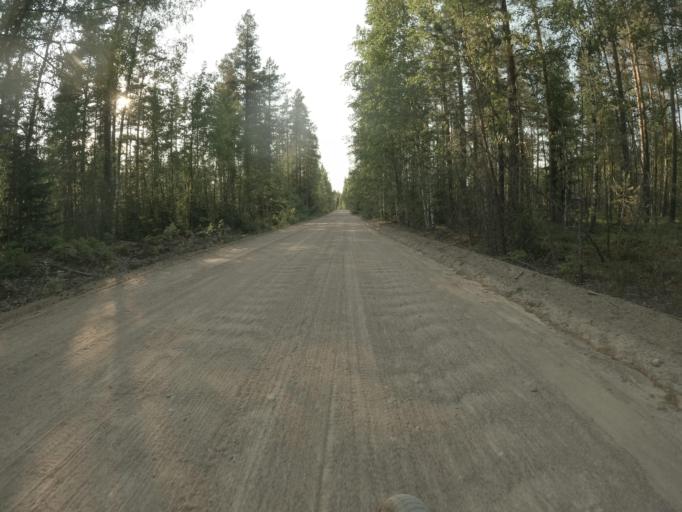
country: RU
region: Leningrad
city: Veshchevo
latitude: 60.4602
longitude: 29.2438
